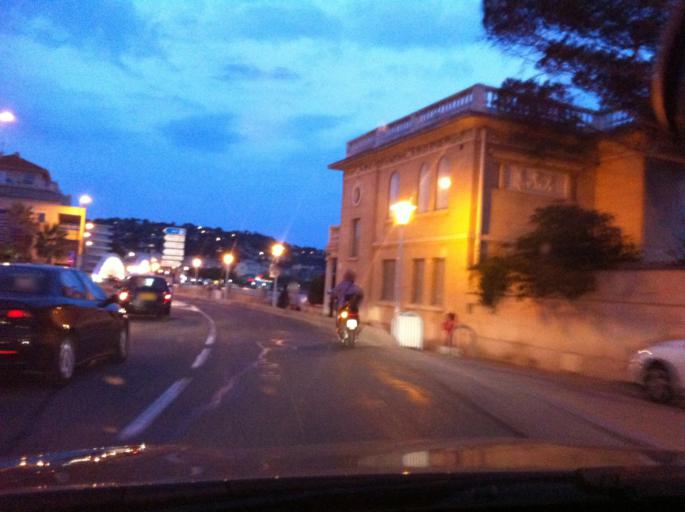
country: FR
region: Provence-Alpes-Cote d'Azur
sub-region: Departement du Var
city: Sainte-Maxime
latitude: 43.3055
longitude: 6.6319
